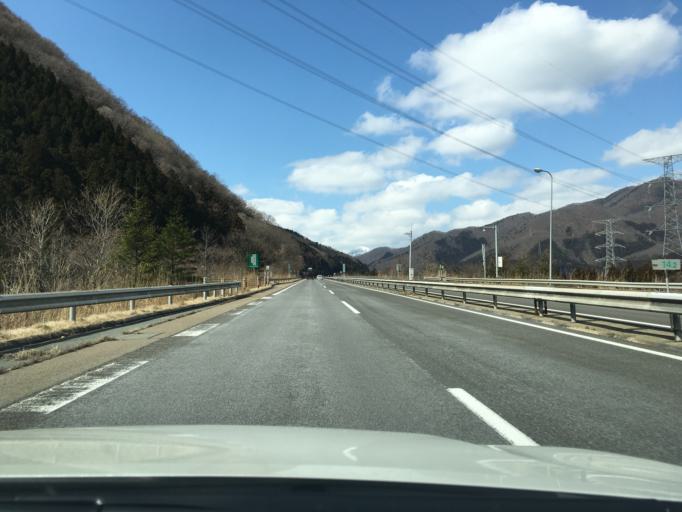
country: JP
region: Miyagi
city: Shiroishi
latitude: 38.1966
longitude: 140.5905
